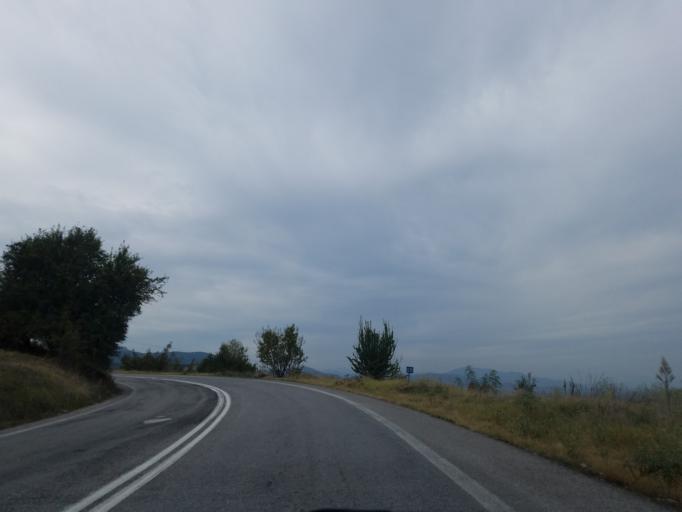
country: GR
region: Central Greece
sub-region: Nomos Fthiotidos
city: Domokos
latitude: 39.1571
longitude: 22.2966
